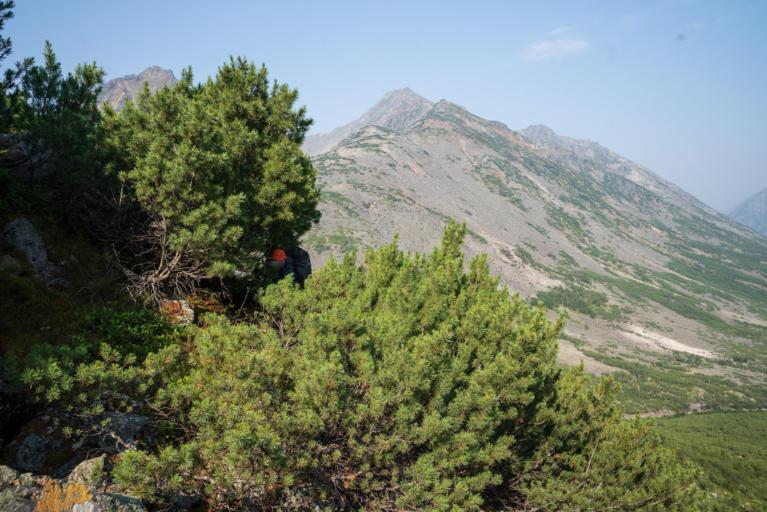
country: RU
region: Transbaikal Territory
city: Kuanda
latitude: 56.8015
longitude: 116.8499
